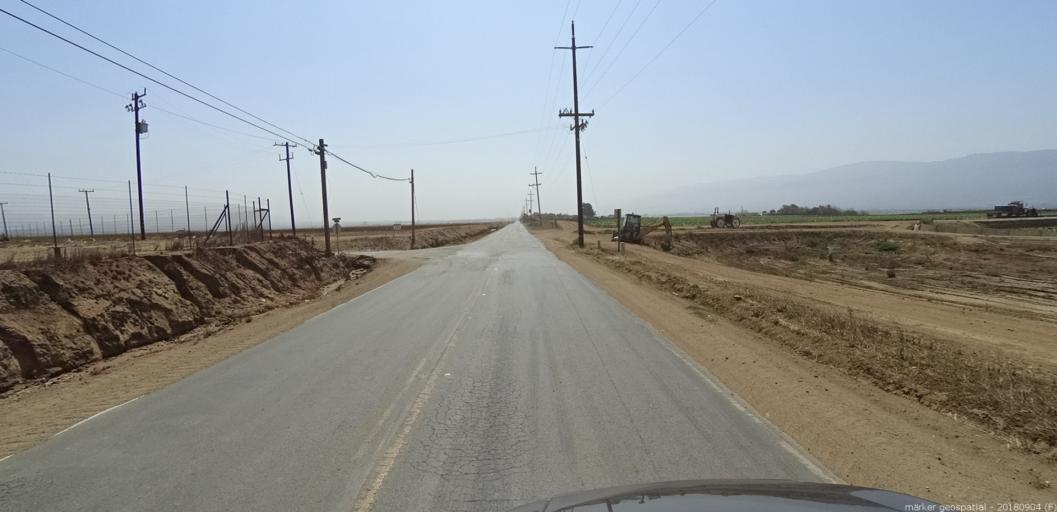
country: US
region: California
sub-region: Monterey County
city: Chualar
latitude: 36.5574
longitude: -121.4787
